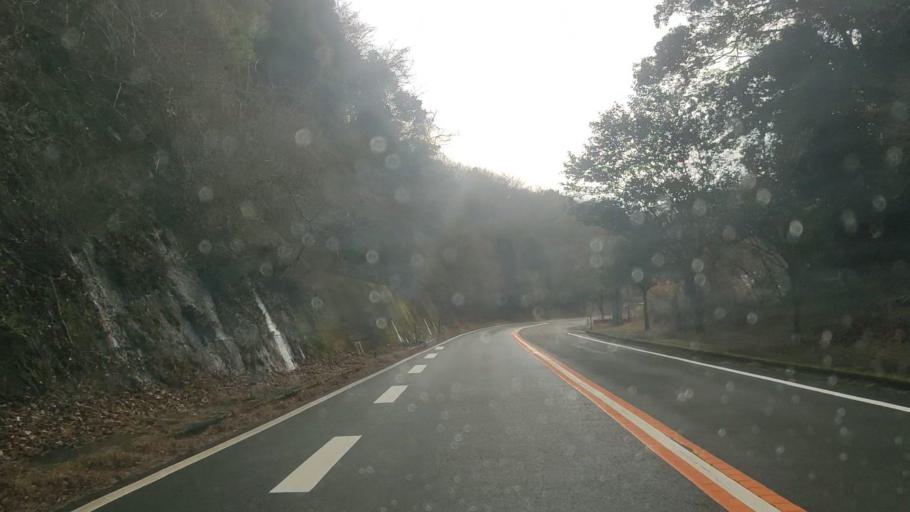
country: JP
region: Kumamoto
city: Hitoyoshi
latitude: 32.1098
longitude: 130.8055
